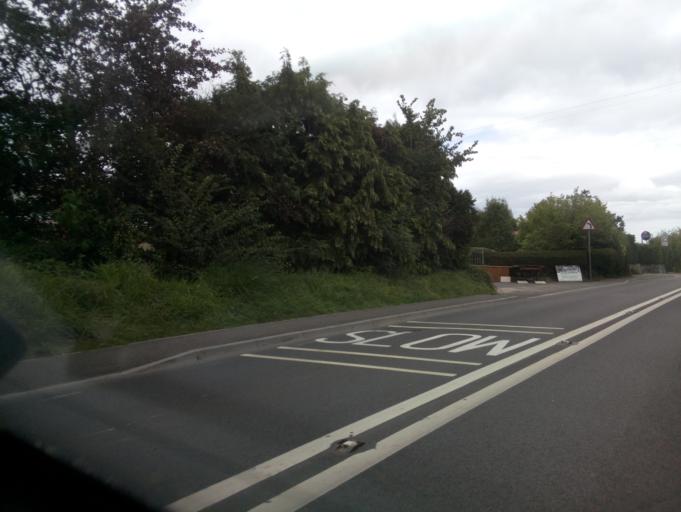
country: GB
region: England
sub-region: Devon
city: Bishopsteignton
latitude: 50.5481
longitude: -3.5429
